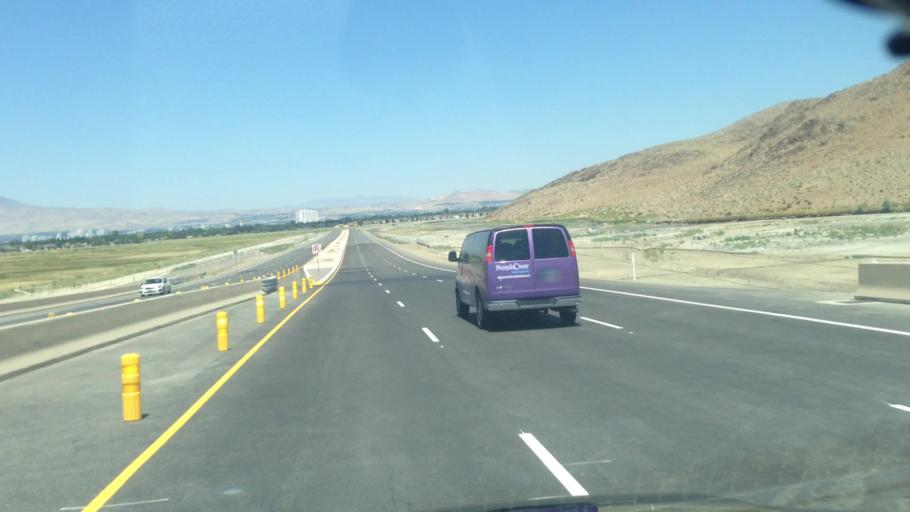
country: US
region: Nevada
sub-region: Washoe County
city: Sparks
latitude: 39.4671
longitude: -119.7304
